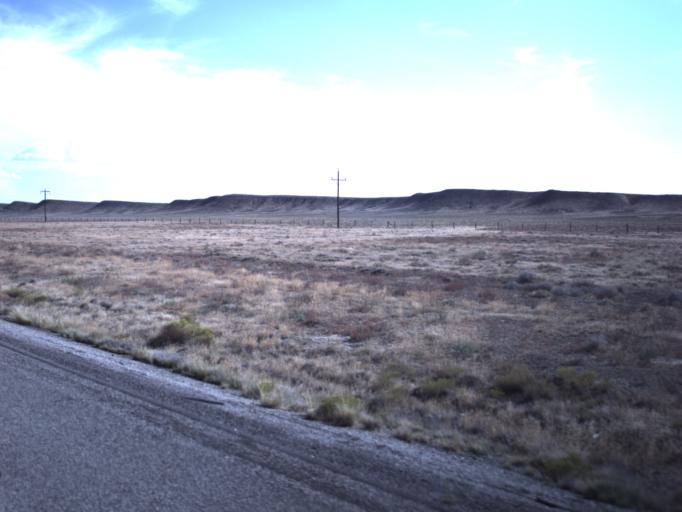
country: US
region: Utah
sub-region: Grand County
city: Moab
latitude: 38.8296
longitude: -109.7853
